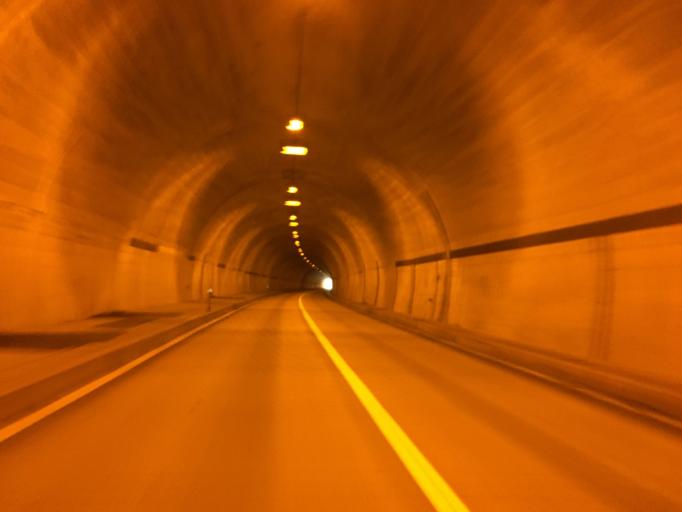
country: JP
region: Fukushima
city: Namie
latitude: 37.5262
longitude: 140.8792
